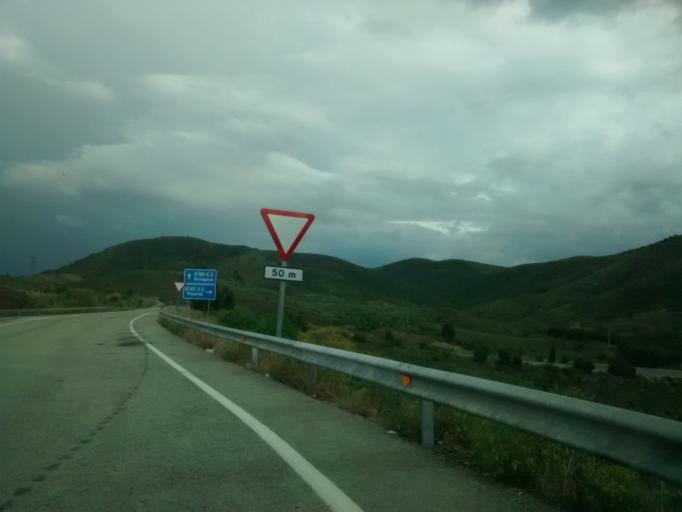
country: ES
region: Aragon
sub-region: Provincia de Zaragoza
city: Ateca
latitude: 41.3229
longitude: -1.7952
